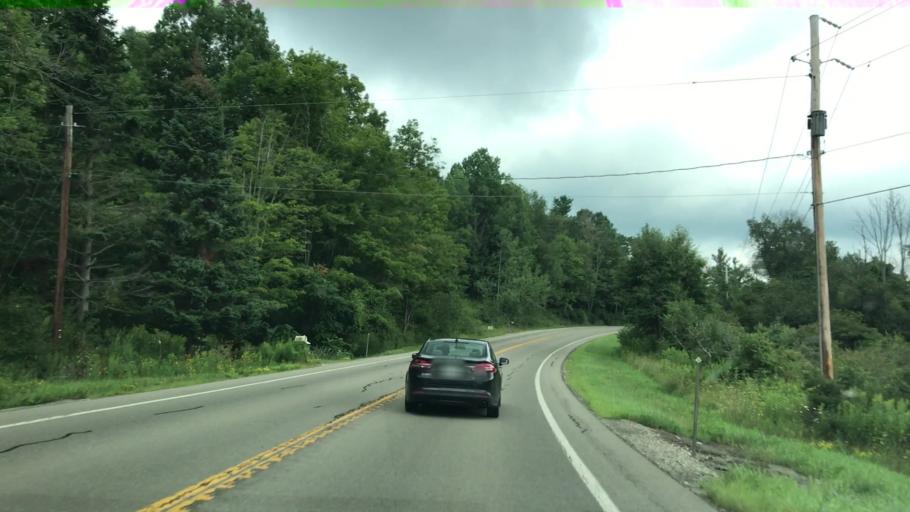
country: US
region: New York
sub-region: Steuben County
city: Bath
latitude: 42.4054
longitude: -77.3515
